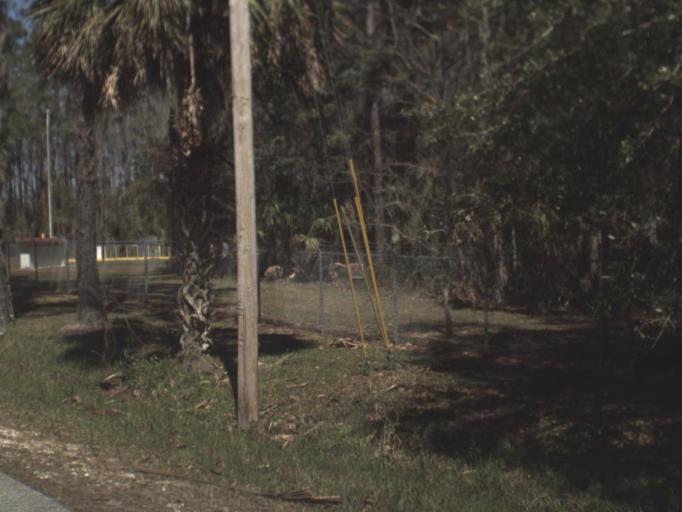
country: US
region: Florida
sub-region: Leon County
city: Woodville
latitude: 30.1620
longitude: -84.2065
